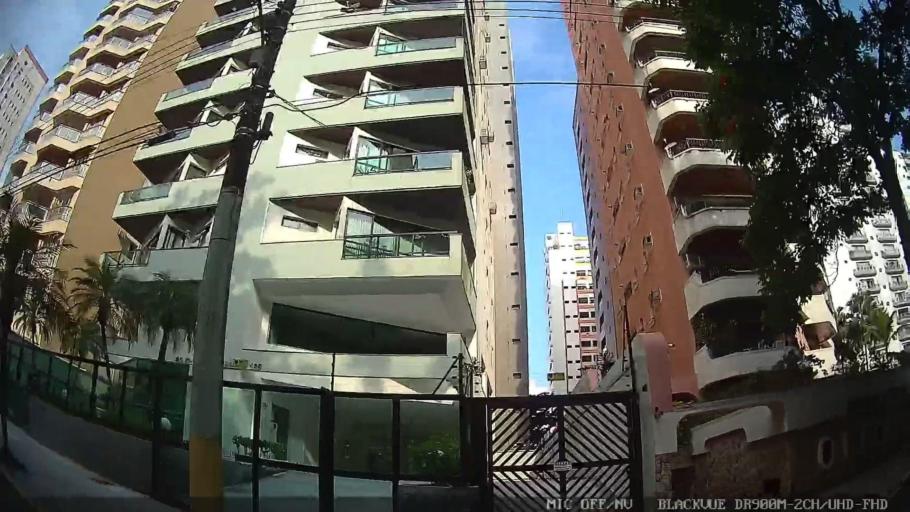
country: BR
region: Sao Paulo
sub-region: Guaruja
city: Guaruja
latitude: -23.9975
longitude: -46.2654
